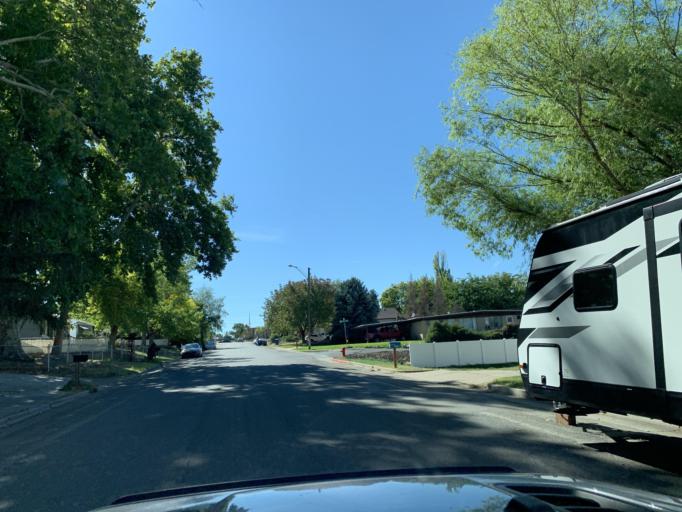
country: US
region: Utah
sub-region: Weber County
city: South Ogden
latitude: 41.1923
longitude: -111.9642
